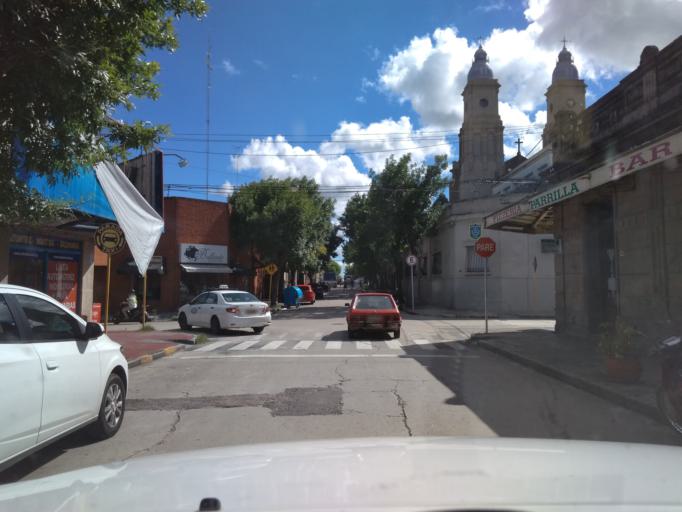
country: UY
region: Florida
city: Florida
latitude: -34.1002
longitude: -56.2131
